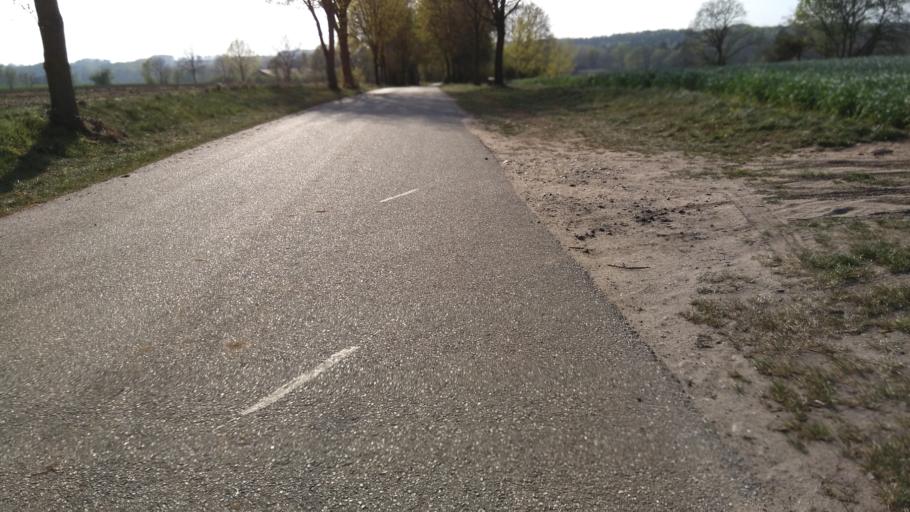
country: DE
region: Lower Saxony
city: Buxtehude
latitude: 53.4366
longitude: 9.6844
